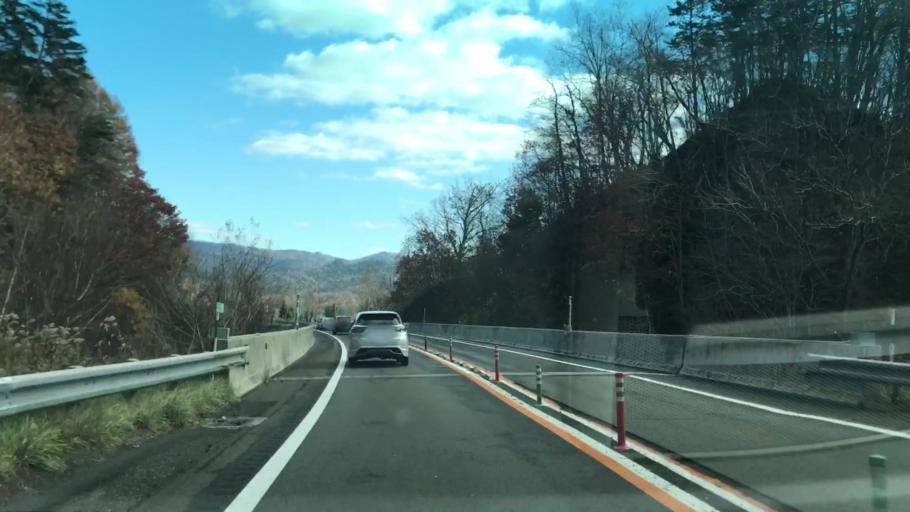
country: JP
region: Hokkaido
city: Chitose
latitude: 42.9094
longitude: 141.9820
